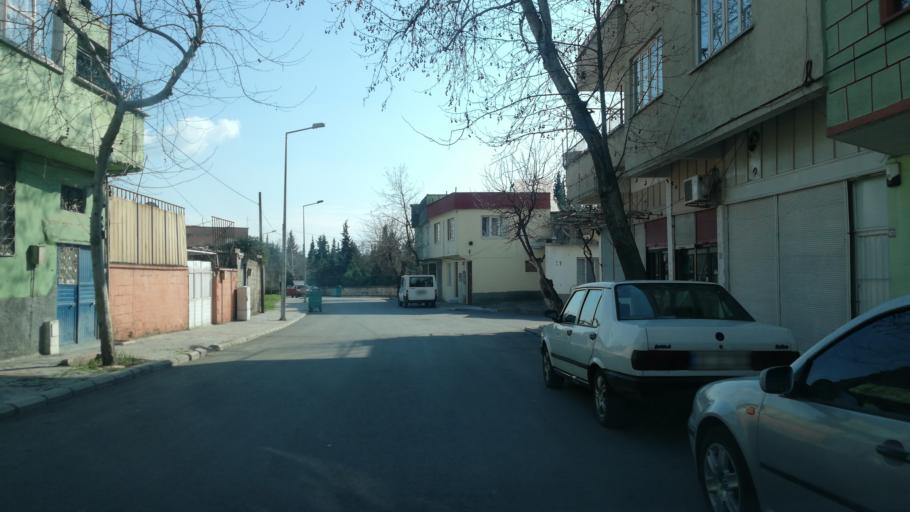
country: TR
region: Kahramanmaras
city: Kahramanmaras
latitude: 37.5790
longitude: 36.9373
